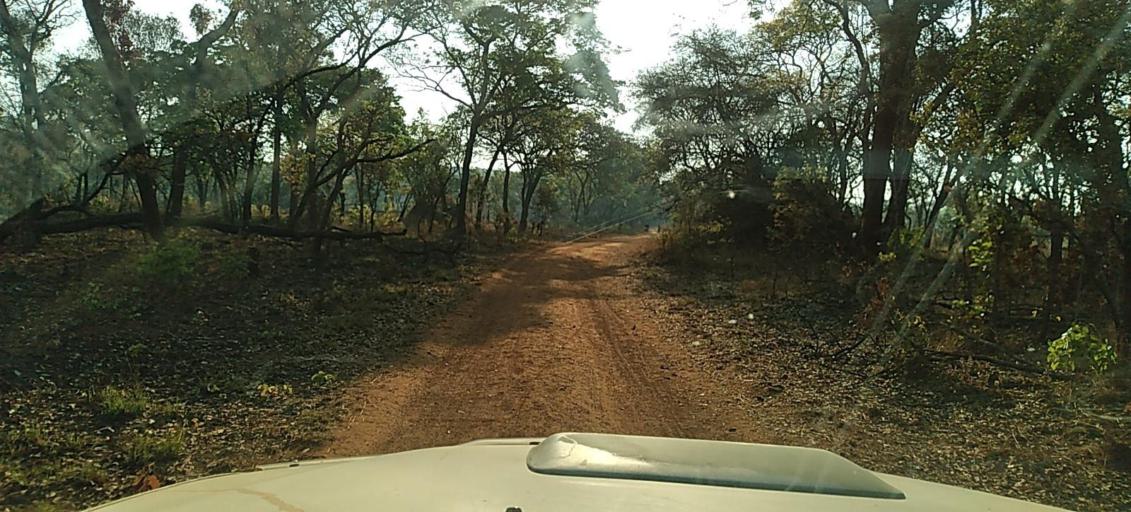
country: ZM
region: North-Western
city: Kasempa
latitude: -13.1672
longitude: 25.8879
